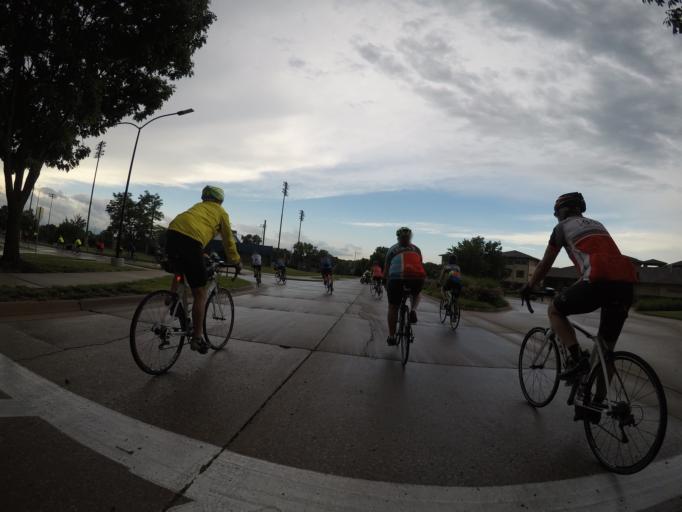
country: US
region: Kansas
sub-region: Shawnee County
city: Topeka
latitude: 39.0319
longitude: -95.7040
